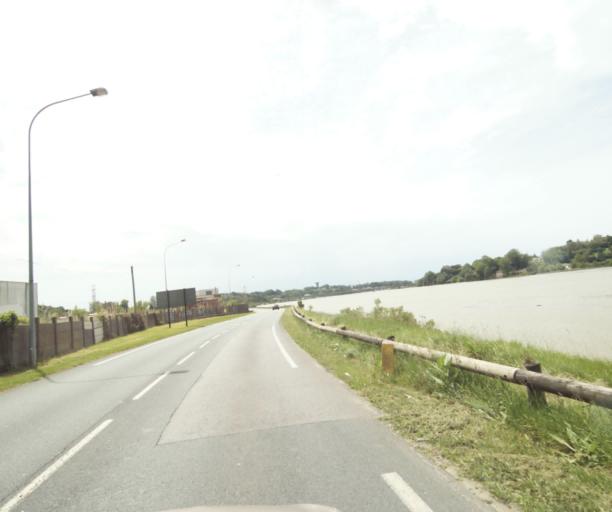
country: FR
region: Aquitaine
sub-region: Departement des Pyrenees-Atlantiques
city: Mouguerre
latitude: 43.4878
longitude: -1.4354
